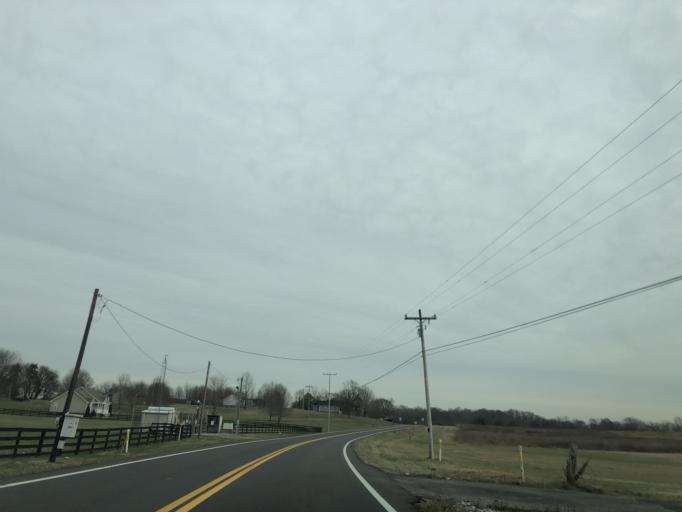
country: US
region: Tennessee
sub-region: Sumner County
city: White House
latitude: 36.4762
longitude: -86.7195
